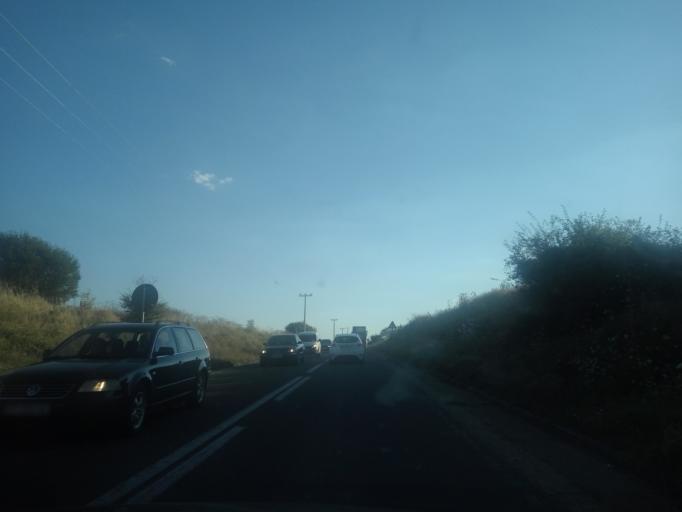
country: XK
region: Gjakova
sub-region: Komuna e Gjakoves
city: Gjakove
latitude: 42.4559
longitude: 20.5059
